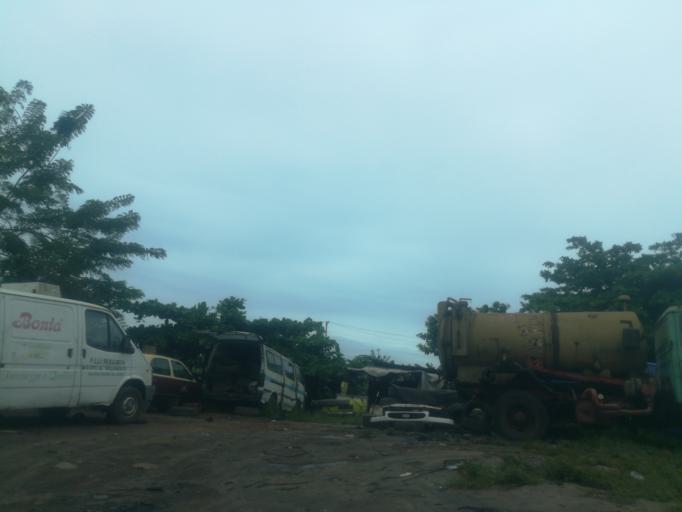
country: NG
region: Oyo
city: Ibadan
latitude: 7.3329
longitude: 3.8790
